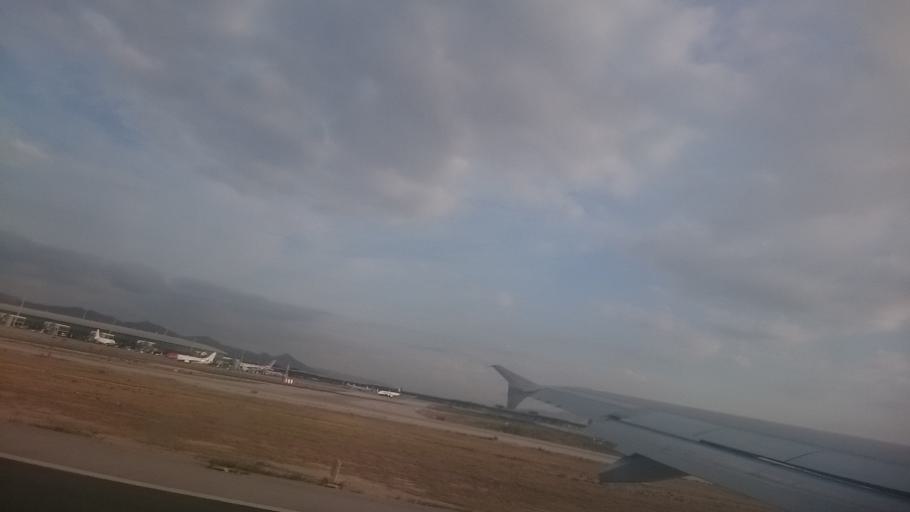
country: ES
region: Catalonia
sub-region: Provincia de Barcelona
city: El Prat de Llobregat
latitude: 41.2871
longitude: 2.0881
